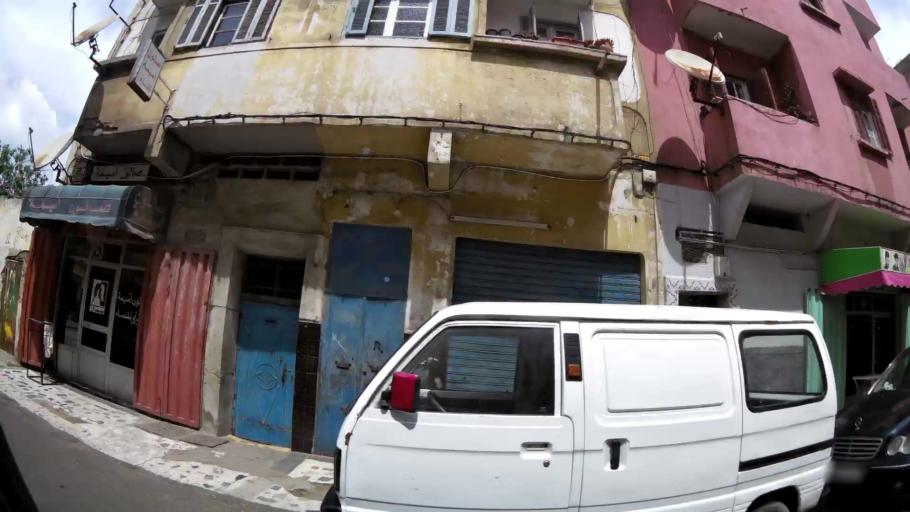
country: MA
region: Grand Casablanca
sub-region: Casablanca
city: Casablanca
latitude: 33.5938
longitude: -7.5778
